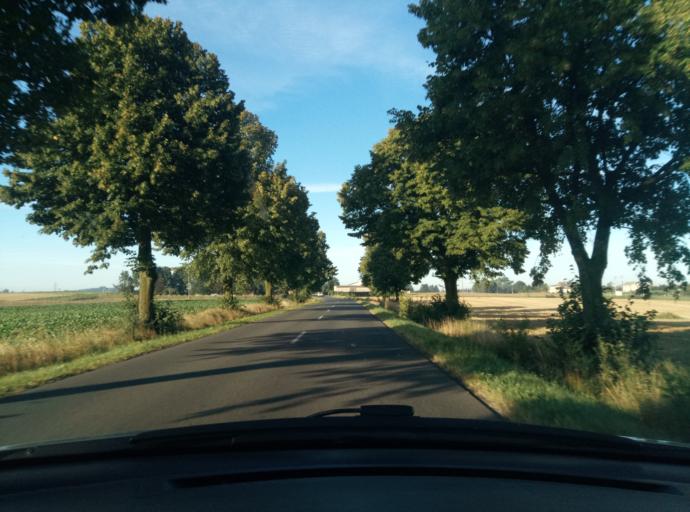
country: PL
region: Kujawsko-Pomorskie
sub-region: Powiat golubsko-dobrzynski
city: Kowalewo Pomorskie
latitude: 53.2060
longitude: 18.9205
